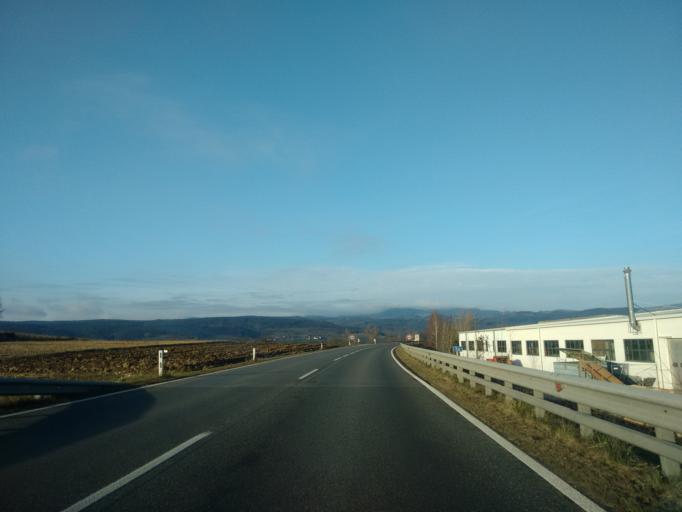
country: AT
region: Lower Austria
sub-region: Politischer Bezirk Melk
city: Emmersdorf an der Donau
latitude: 48.2302
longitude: 15.3481
